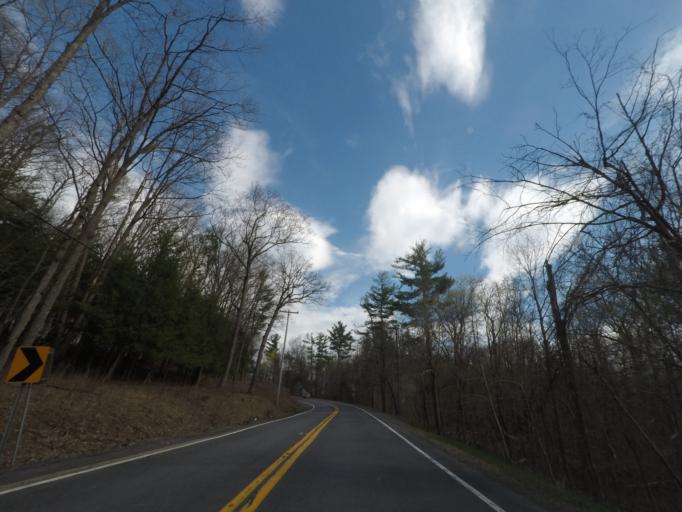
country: US
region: New York
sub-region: Albany County
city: Voorheesville
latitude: 42.5714
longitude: -73.9143
